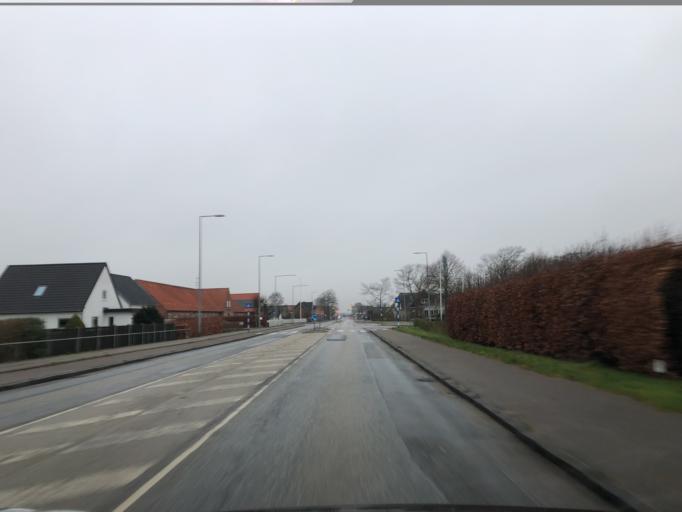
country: DK
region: Central Jutland
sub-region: Herning Kommune
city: Lind
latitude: 56.1025
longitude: 8.9797
